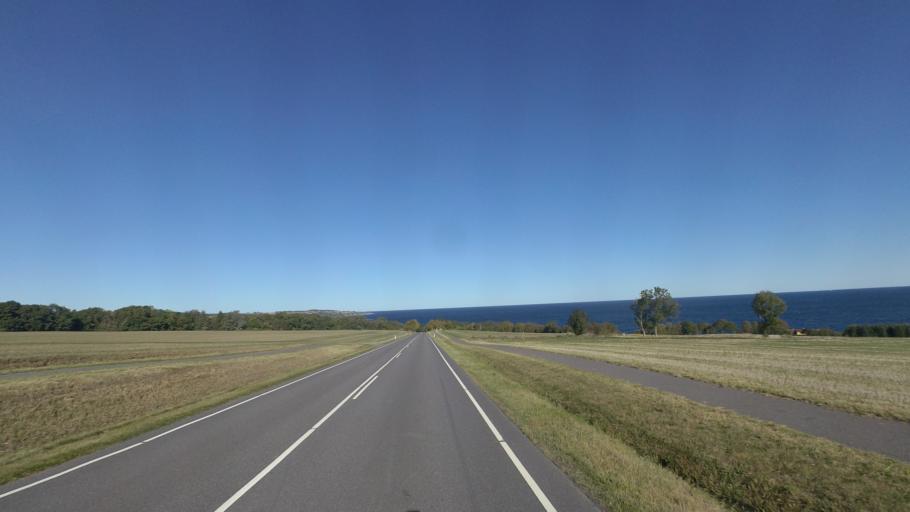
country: DK
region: Capital Region
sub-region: Bornholm Kommune
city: Akirkeby
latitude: 55.1701
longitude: 15.0276
